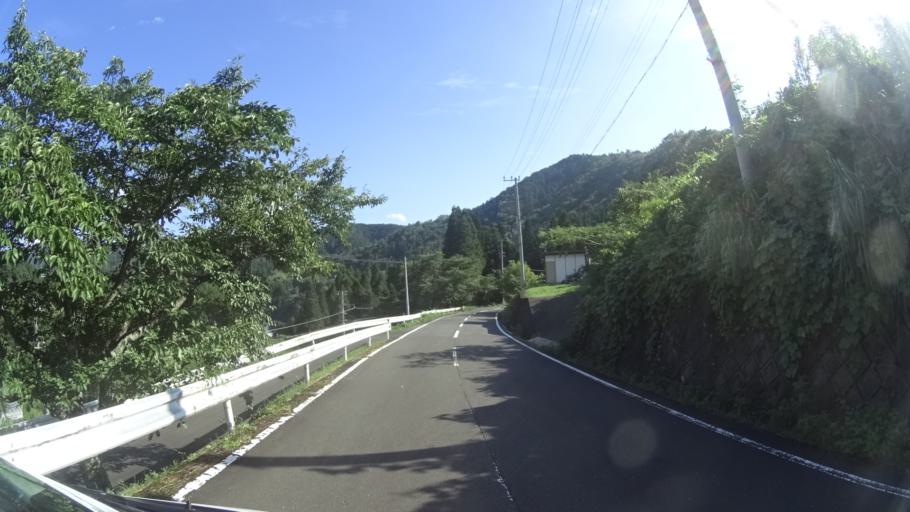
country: JP
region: Kyoto
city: Ayabe
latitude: 35.2811
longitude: 135.3314
